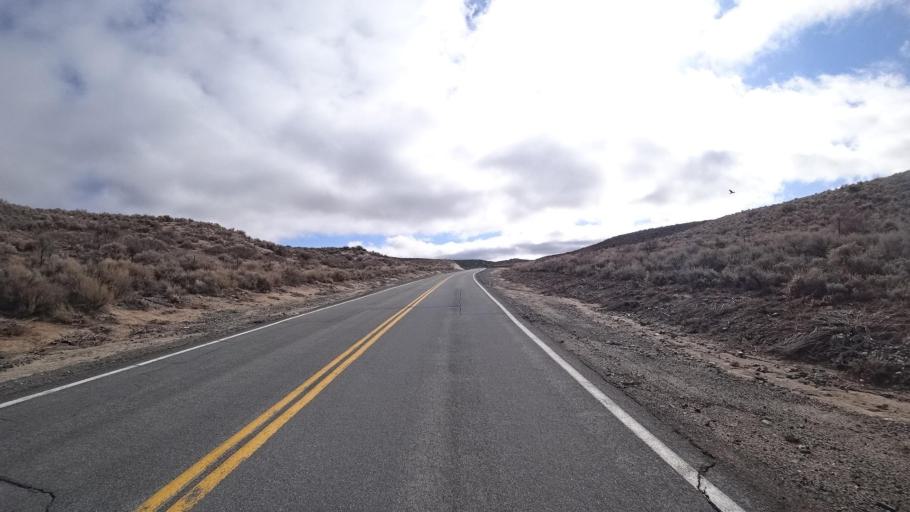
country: US
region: Nevada
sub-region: Washoe County
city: Cold Springs
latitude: 39.8043
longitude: -119.9241
